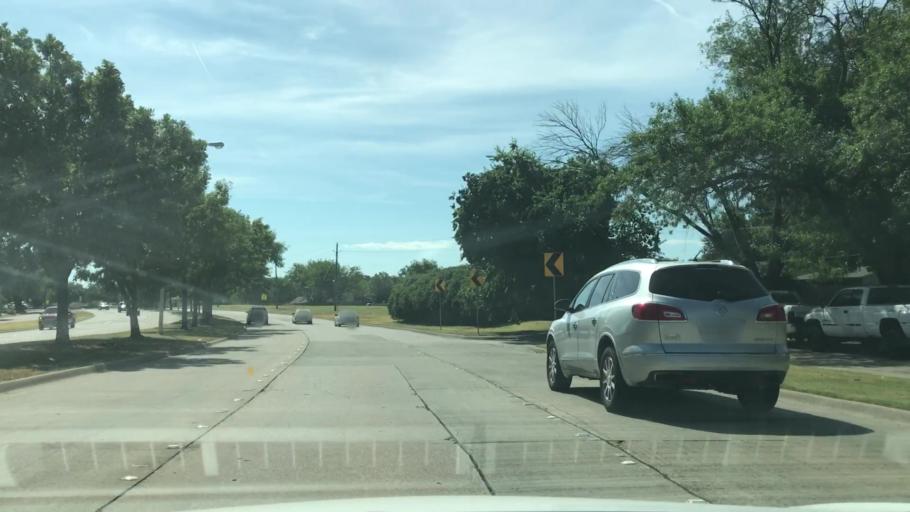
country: US
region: Texas
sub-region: Collin County
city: Plano
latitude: 33.0562
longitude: -96.7264
